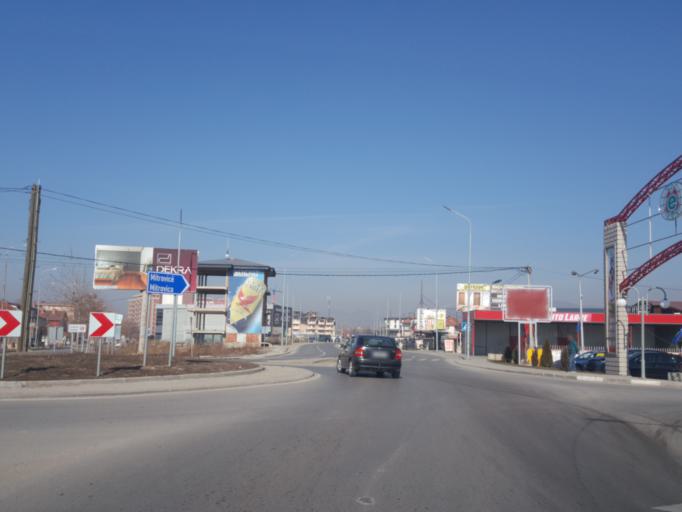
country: XK
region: Mitrovica
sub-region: Vushtrri
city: Vushtrri
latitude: 42.8149
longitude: 20.9833
